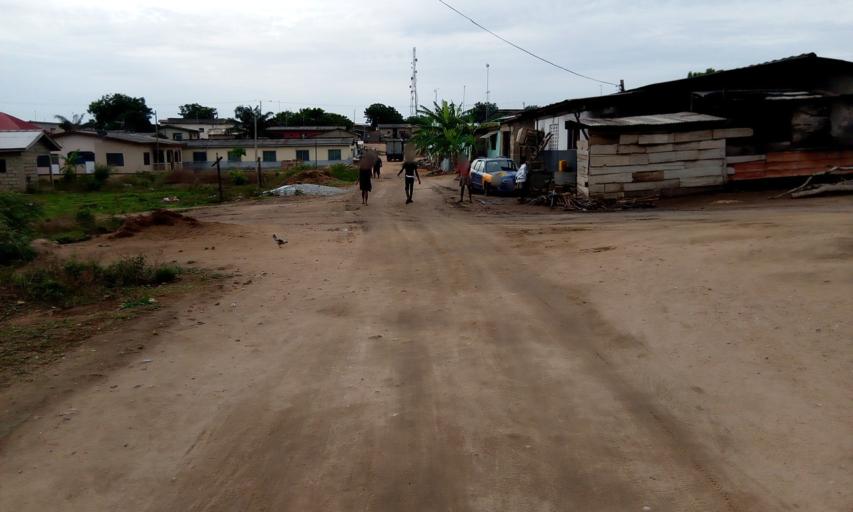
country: GH
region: Central
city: Winneba
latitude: 5.3571
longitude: -0.6203
